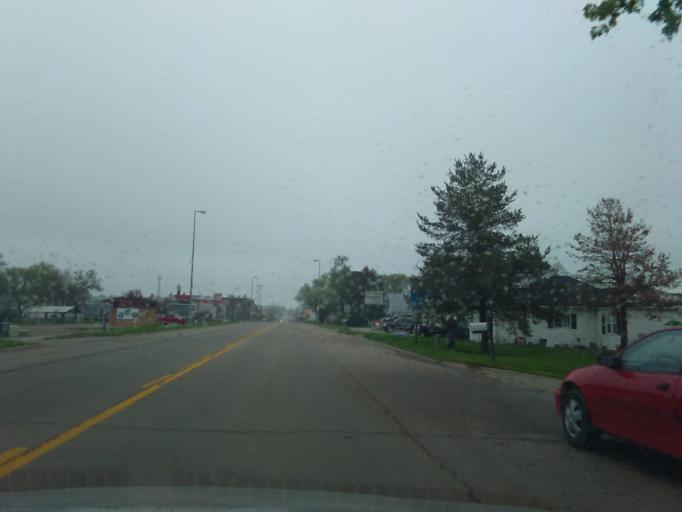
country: US
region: Nebraska
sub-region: Wayne County
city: Wayne
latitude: 42.2252
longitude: -97.0178
